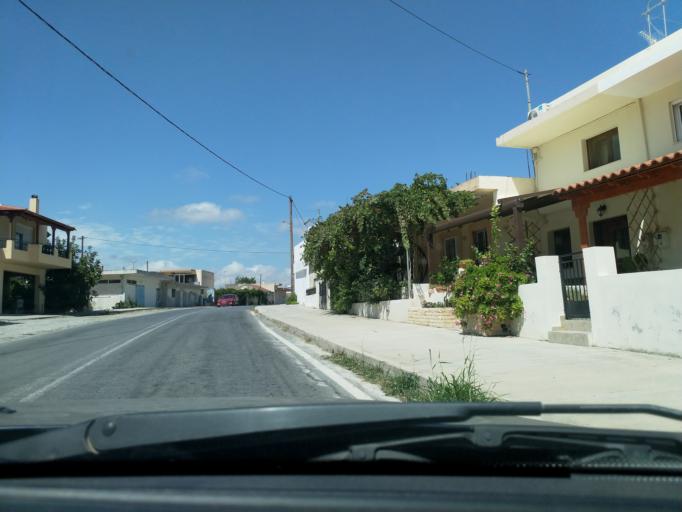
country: GR
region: Crete
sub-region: Nomos Rethymnis
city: Agia Foteini
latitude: 35.1863
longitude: 24.5552
